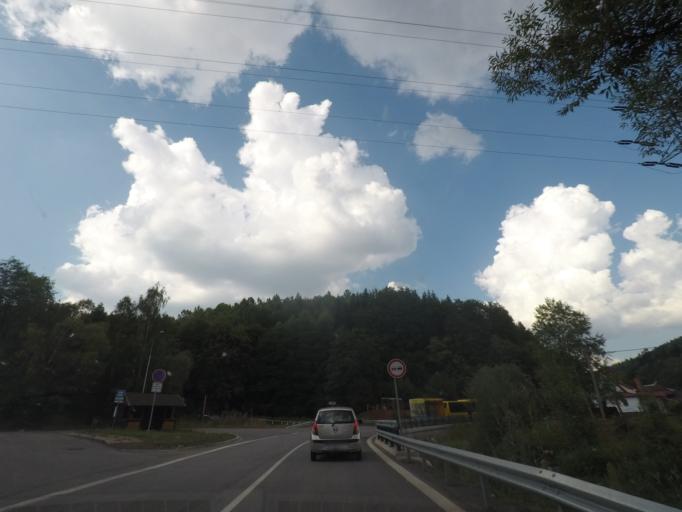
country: CZ
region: Kralovehradecky
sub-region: Okres Trutnov
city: Trutnov
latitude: 50.5795
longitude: 15.9653
